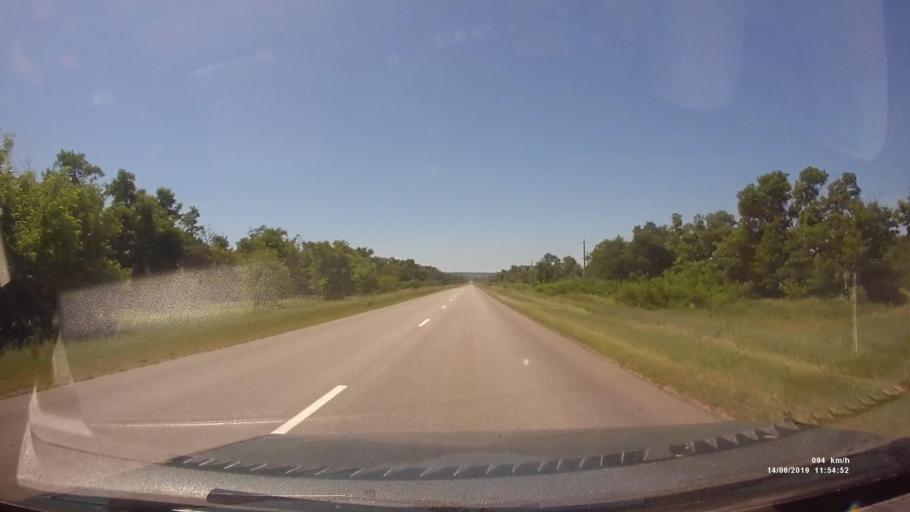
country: RU
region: Rostov
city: Kazanskaya
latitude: 49.8154
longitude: 41.1870
